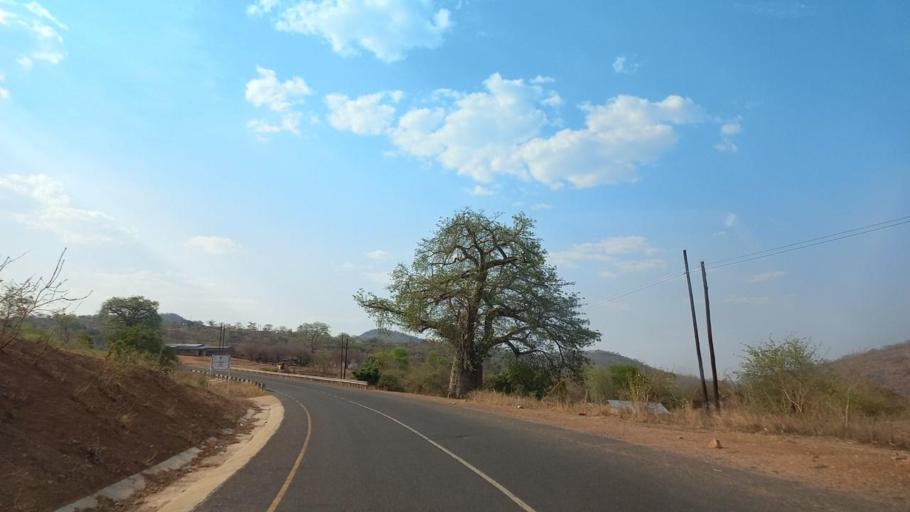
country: ZM
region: Lusaka
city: Luangwa
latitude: -14.9898
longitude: 30.2126
